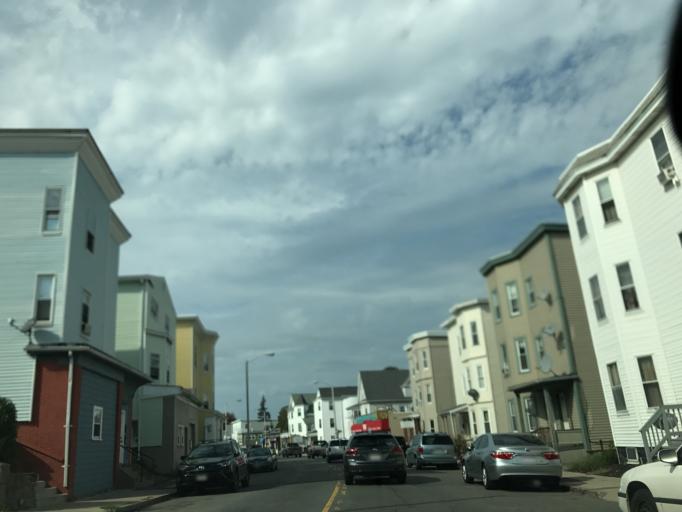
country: US
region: Massachusetts
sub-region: Middlesex County
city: Everett
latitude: 42.4173
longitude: -71.0495
